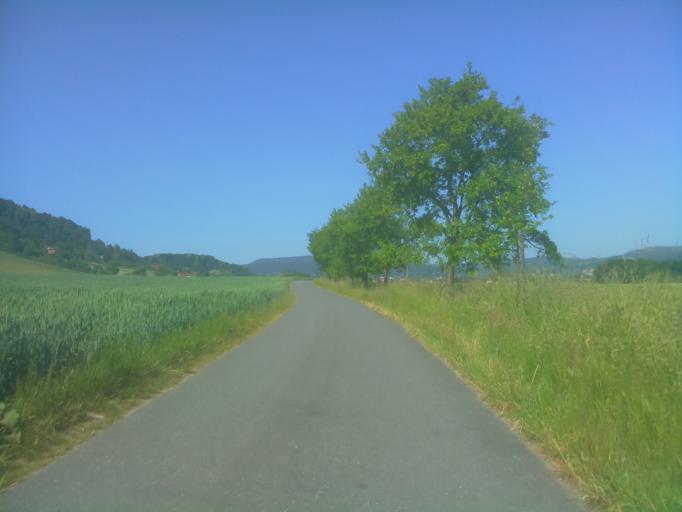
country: DE
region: Thuringia
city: Rudolstadt
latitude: 50.7121
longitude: 11.3604
